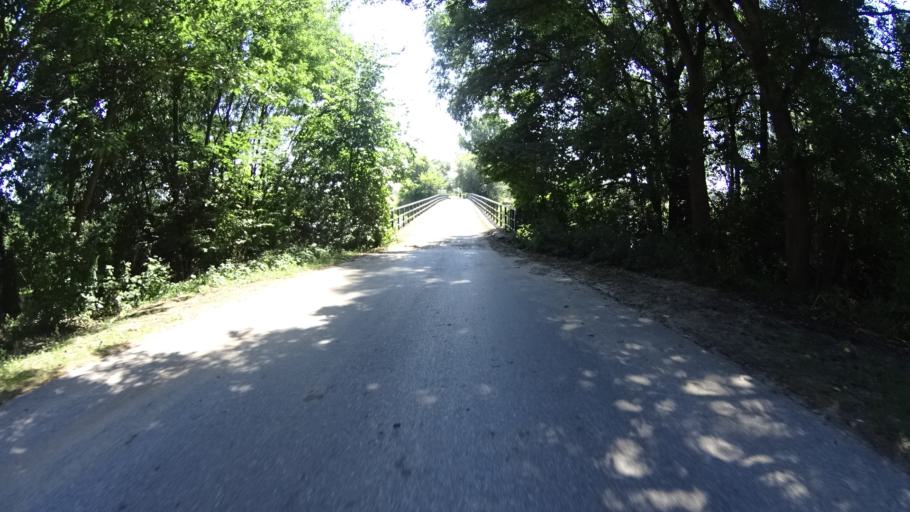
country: PL
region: Masovian Voivodeship
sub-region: Powiat bialobrzeski
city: Bialobrzegi
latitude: 51.6660
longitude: 20.9177
